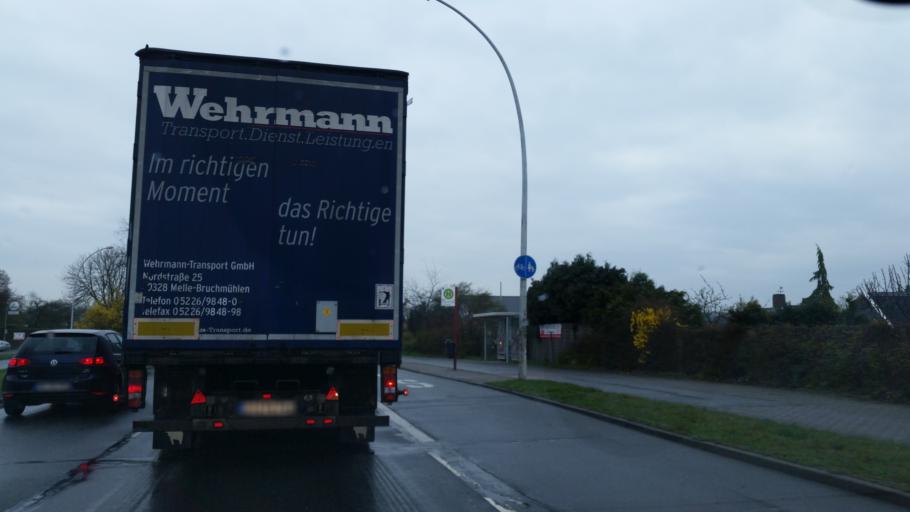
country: DE
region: Lower Saxony
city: Wolfsburg
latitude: 52.4257
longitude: 10.7579
